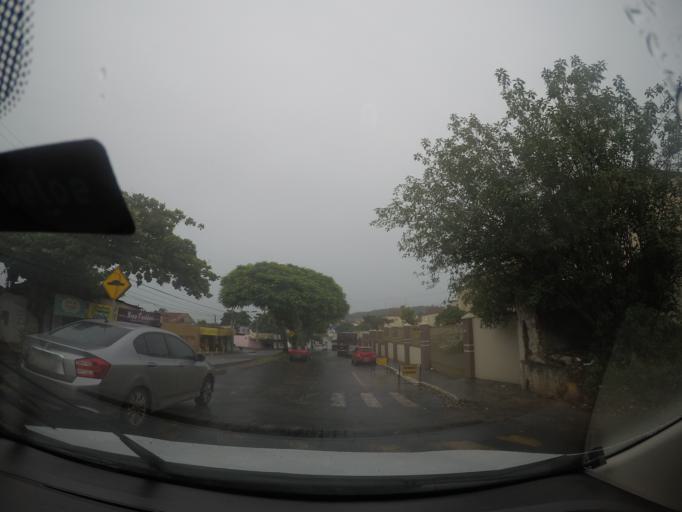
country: BR
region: Goias
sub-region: Goiania
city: Goiania
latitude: -16.6750
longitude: -49.3183
